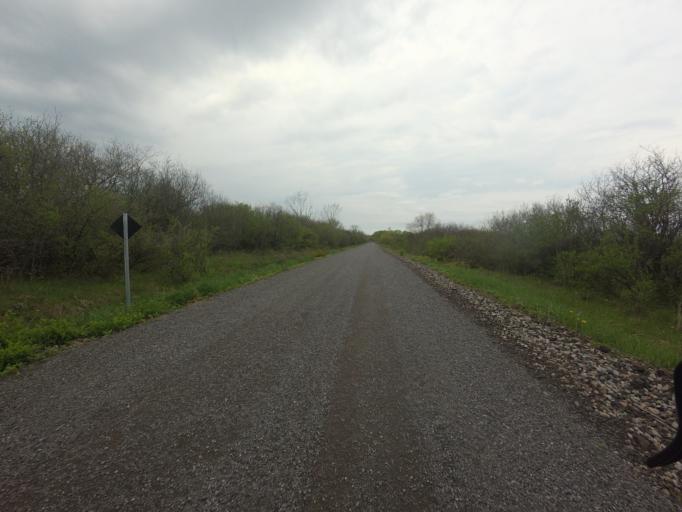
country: CA
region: Ontario
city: Carleton Place
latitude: 45.2171
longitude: -76.1836
